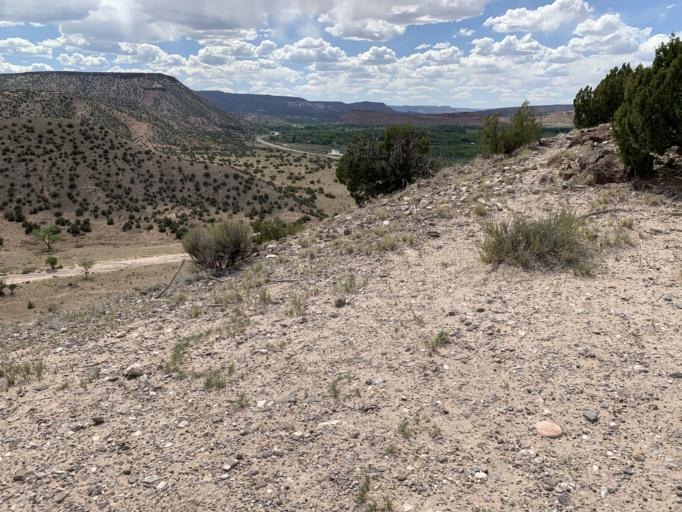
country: US
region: New Mexico
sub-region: Rio Arriba County
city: Ohkay Owingeh
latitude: 36.2103
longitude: -106.2752
